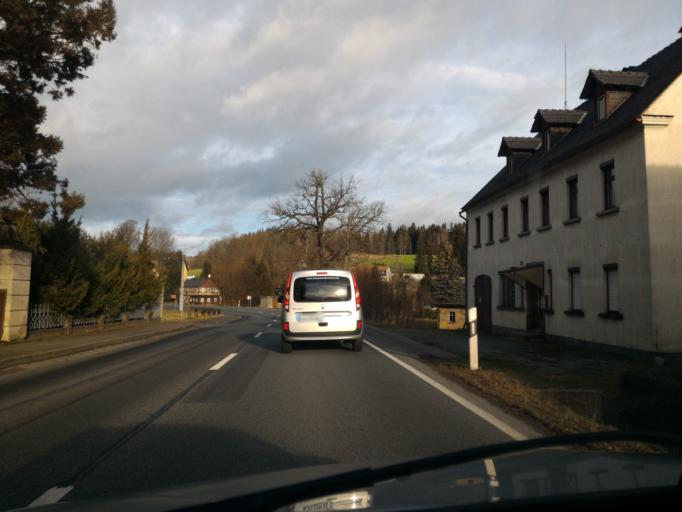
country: DE
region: Saxony
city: Friedersdorf
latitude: 51.0333
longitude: 14.5543
